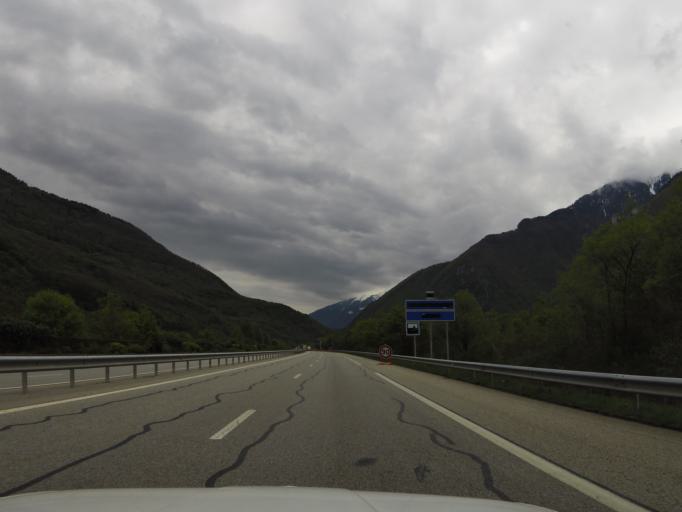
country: FR
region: Rhone-Alpes
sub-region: Departement de la Savoie
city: Saint-Remy-de-Maurienne
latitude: 45.4391
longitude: 6.2834
